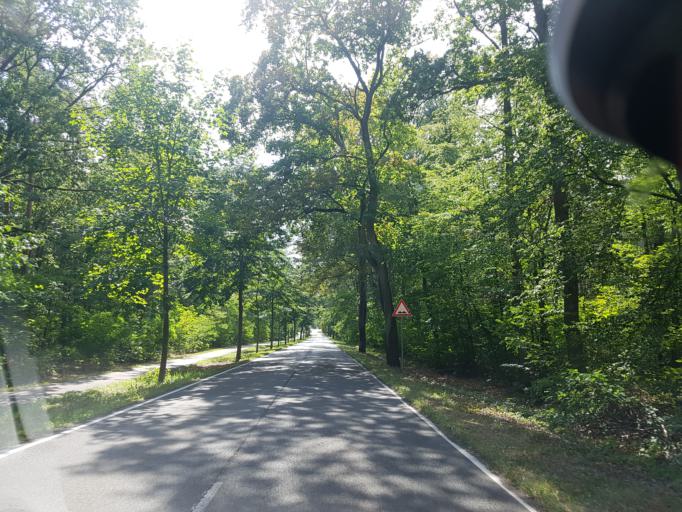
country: DE
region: Brandenburg
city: Gross Kreutz
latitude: 52.3327
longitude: 12.7282
